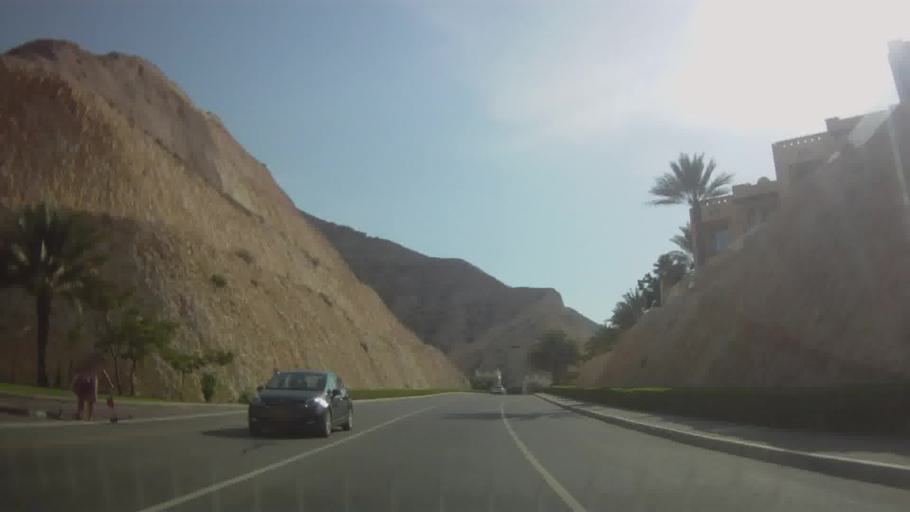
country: OM
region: Muhafazat Masqat
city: Muscat
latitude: 23.5468
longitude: 58.6566
